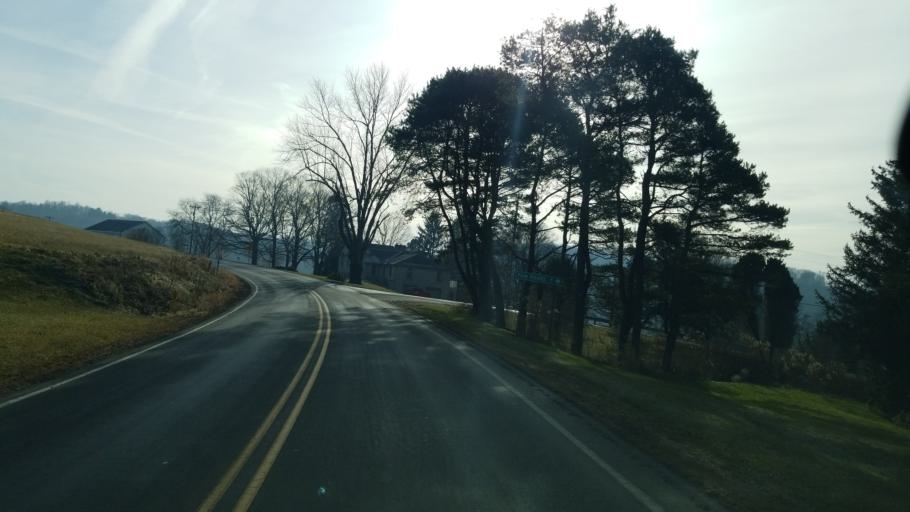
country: US
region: Pennsylvania
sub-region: Indiana County
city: Chevy Chase Heights
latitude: 40.7623
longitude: -79.1462
